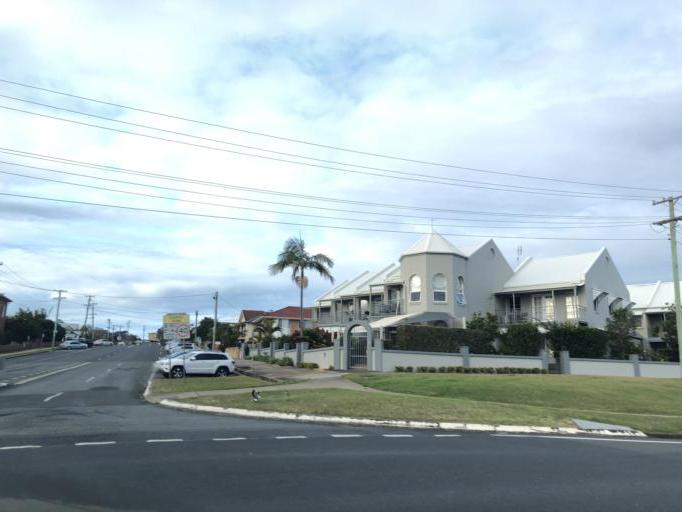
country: AU
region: New South Wales
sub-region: Coffs Harbour
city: Coffs Harbour
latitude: -30.3048
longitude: 153.1348
